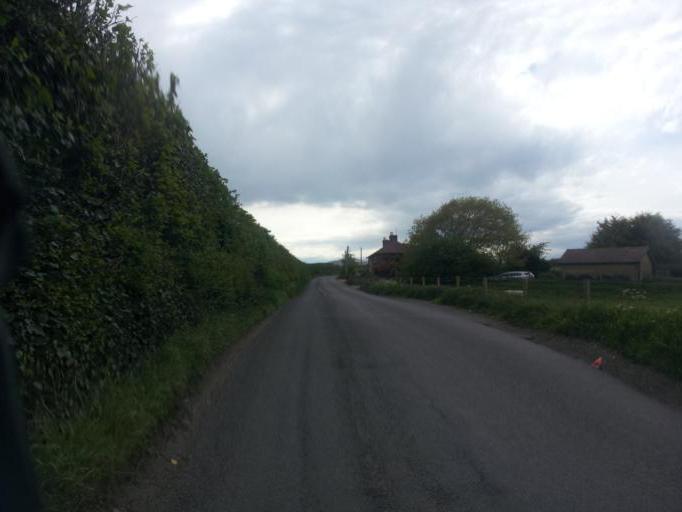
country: GB
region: England
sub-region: Kent
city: Teynham
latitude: 51.3380
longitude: 0.7837
